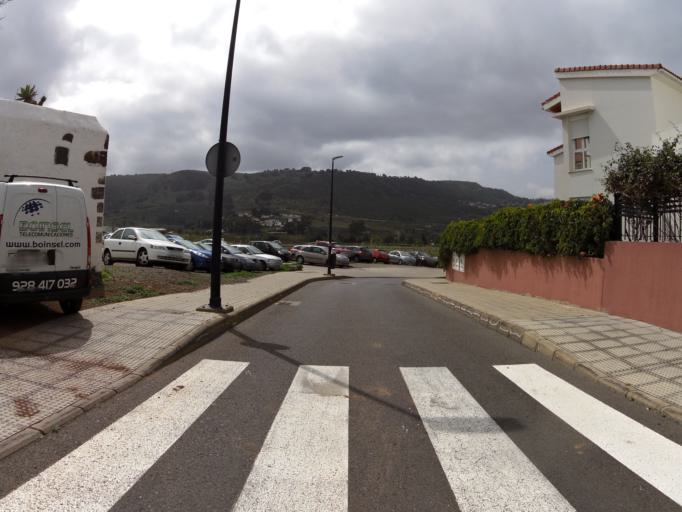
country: ES
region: Canary Islands
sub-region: Provincia de Las Palmas
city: Arucas
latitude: 28.1163
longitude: -15.5214
